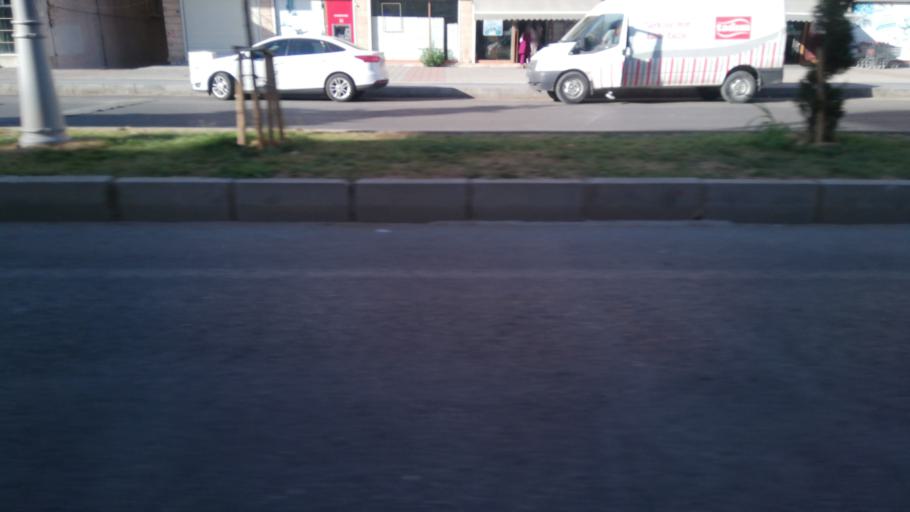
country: TR
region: Mardin
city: Midyat
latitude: 37.4196
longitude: 41.3530
